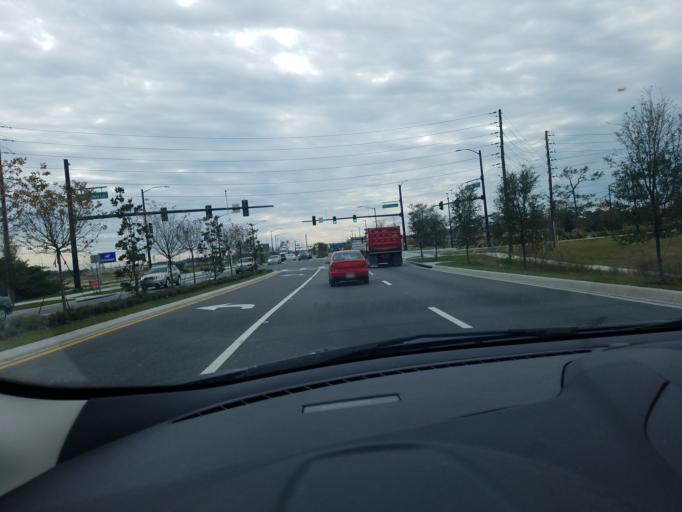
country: US
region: Florida
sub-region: Orange County
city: Hunters Creek
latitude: 28.3487
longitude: -81.3920
